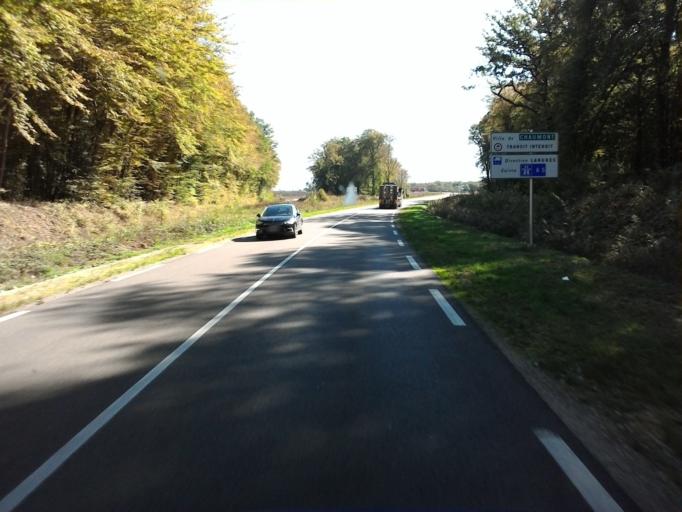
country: FR
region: Champagne-Ardenne
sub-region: Departement de la Haute-Marne
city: Chaumont
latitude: 48.1110
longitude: 5.1026
